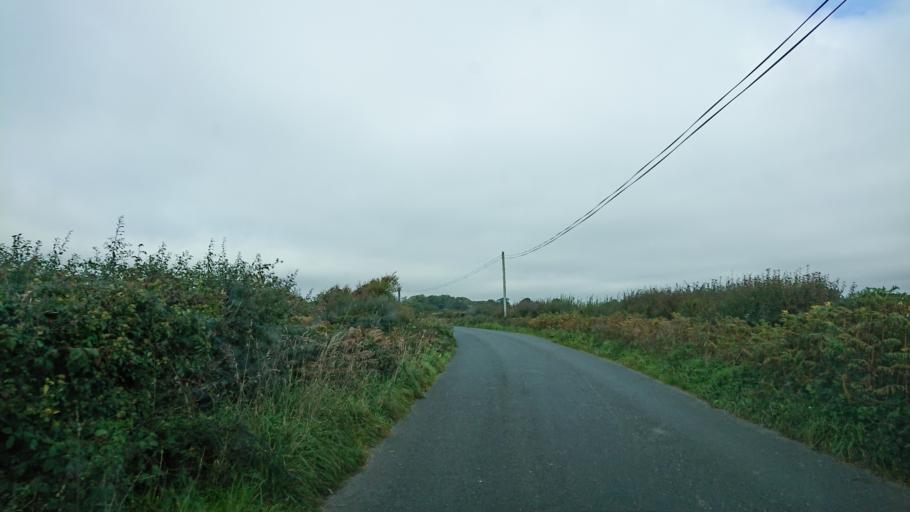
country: IE
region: Munster
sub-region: Waterford
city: Tra Mhor
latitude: 52.1884
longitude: -7.1166
